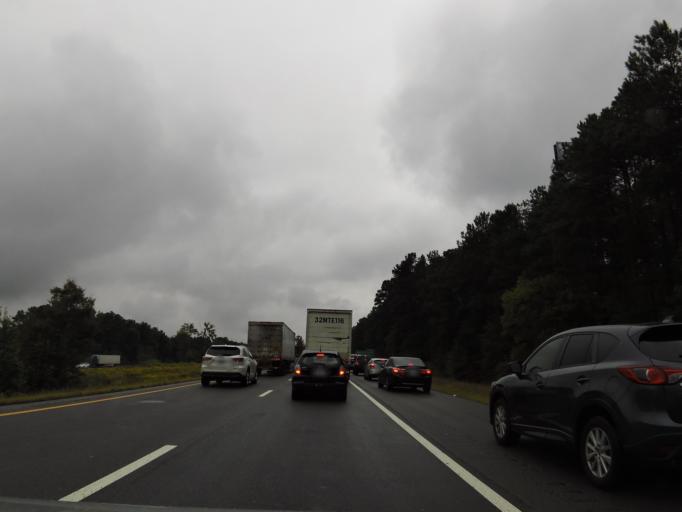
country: US
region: Tennessee
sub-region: Bradley County
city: Hopewell
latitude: 35.2335
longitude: -84.8525
